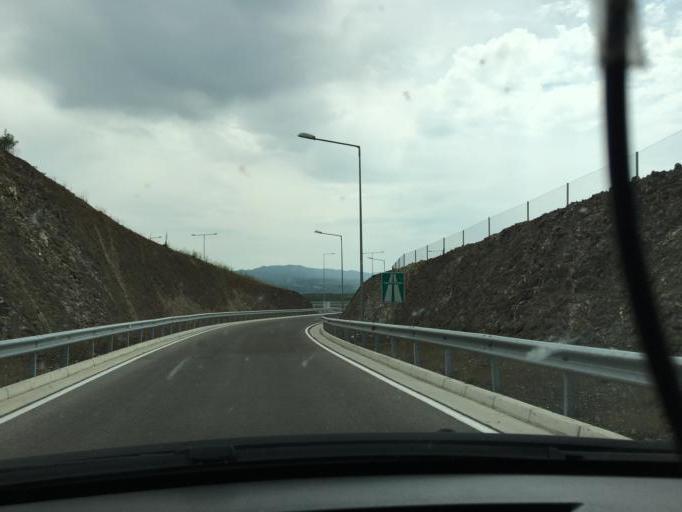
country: MK
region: Gevgelija
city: Miravci
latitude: 41.2956
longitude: 22.4314
